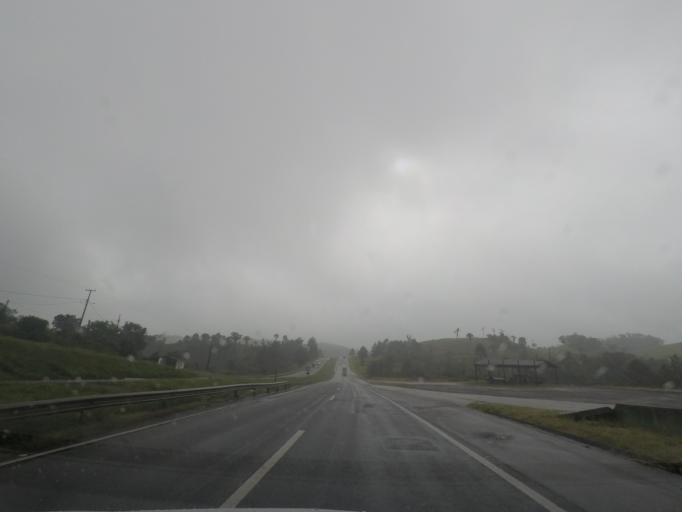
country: BR
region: Parana
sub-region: Antonina
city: Antonina
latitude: -25.0849
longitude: -48.6010
